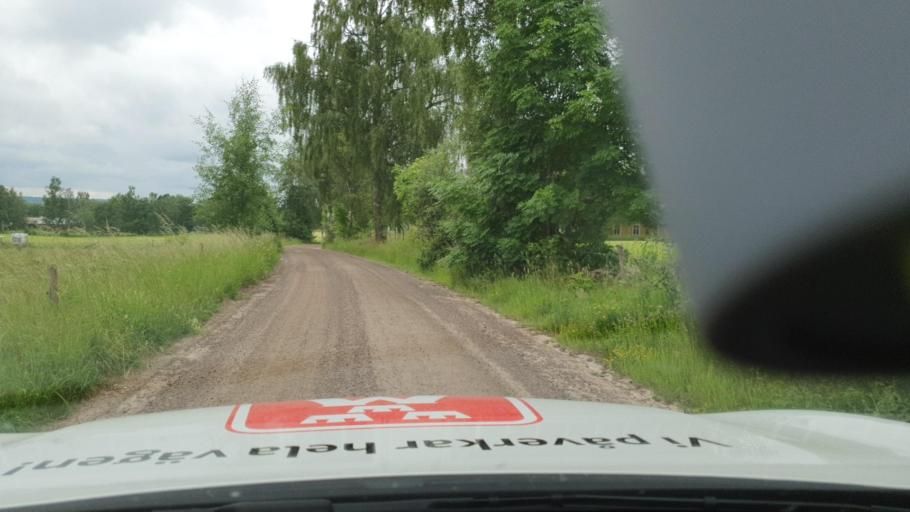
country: SE
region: Vaestra Goetaland
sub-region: Hjo Kommun
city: Hjo
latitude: 58.3380
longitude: 14.2589
